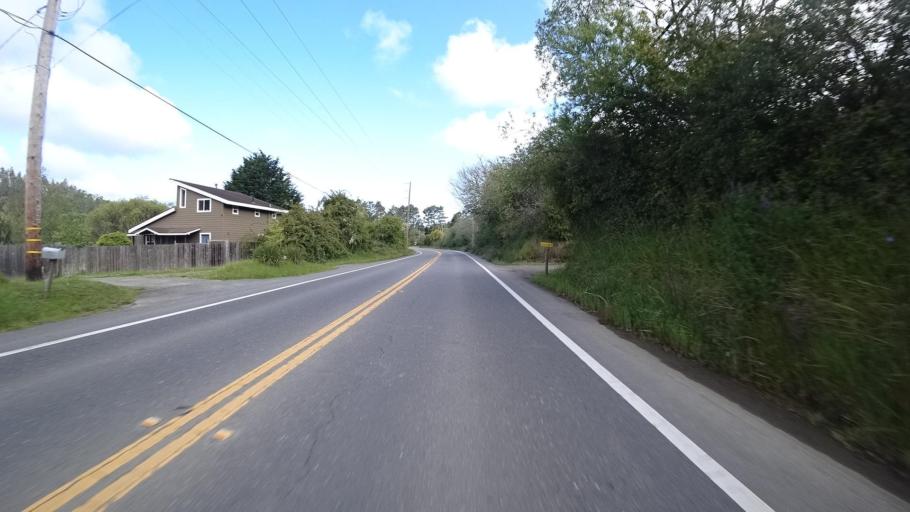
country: US
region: California
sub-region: Humboldt County
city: Myrtletown
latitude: 40.7674
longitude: -124.0684
